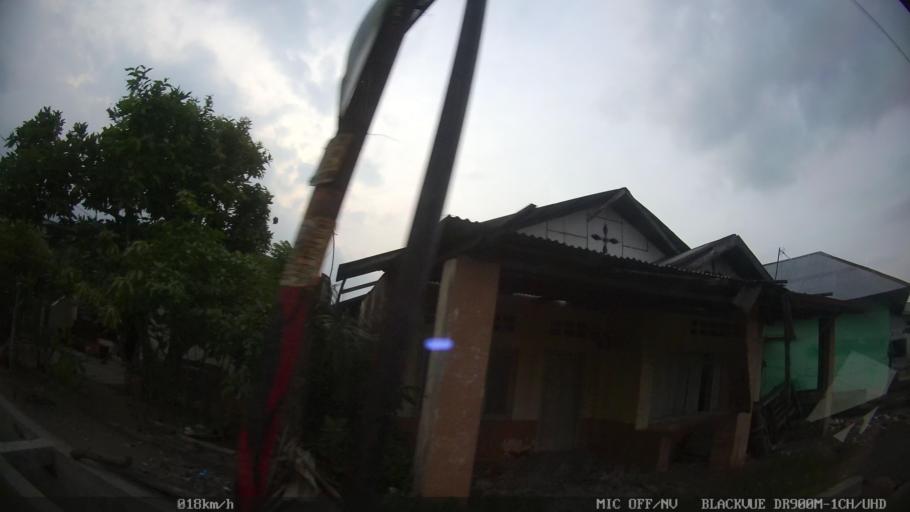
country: ID
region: North Sumatra
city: Sunggal
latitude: 3.5746
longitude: 98.5861
